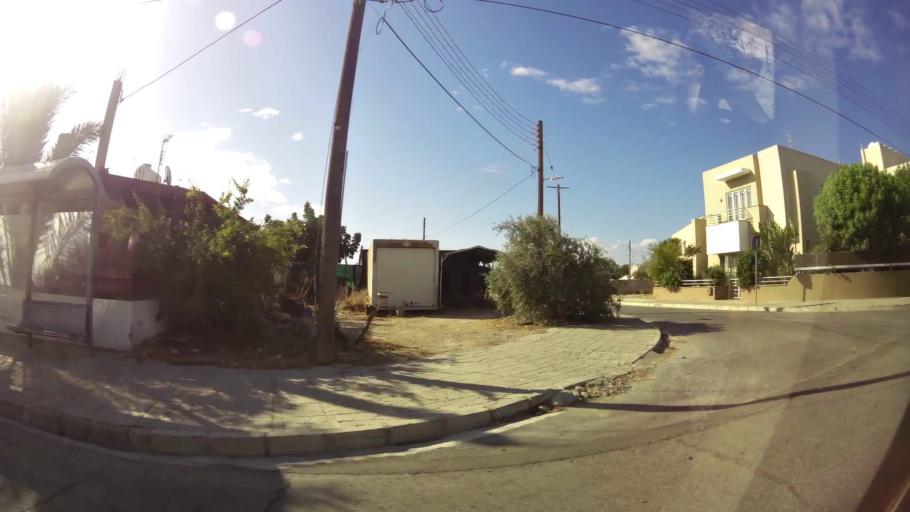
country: CY
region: Lefkosia
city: Nicosia
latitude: 35.1244
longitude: 33.3450
